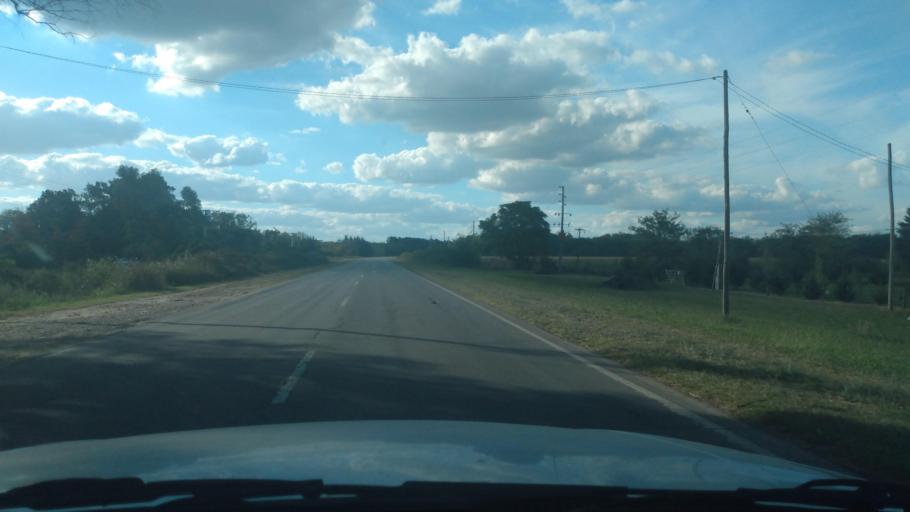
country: AR
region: Buenos Aires
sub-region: Partido de Mercedes
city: Mercedes
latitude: -34.6902
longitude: -59.4046
